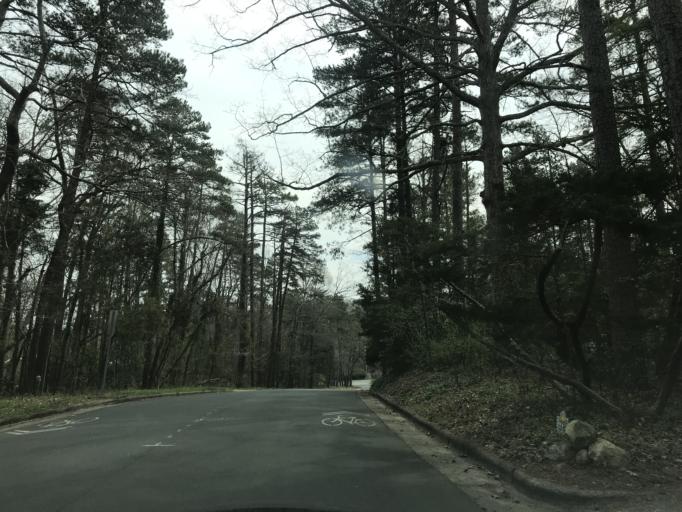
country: US
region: North Carolina
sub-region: Orange County
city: Chapel Hill
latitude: 35.9020
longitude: -79.0351
